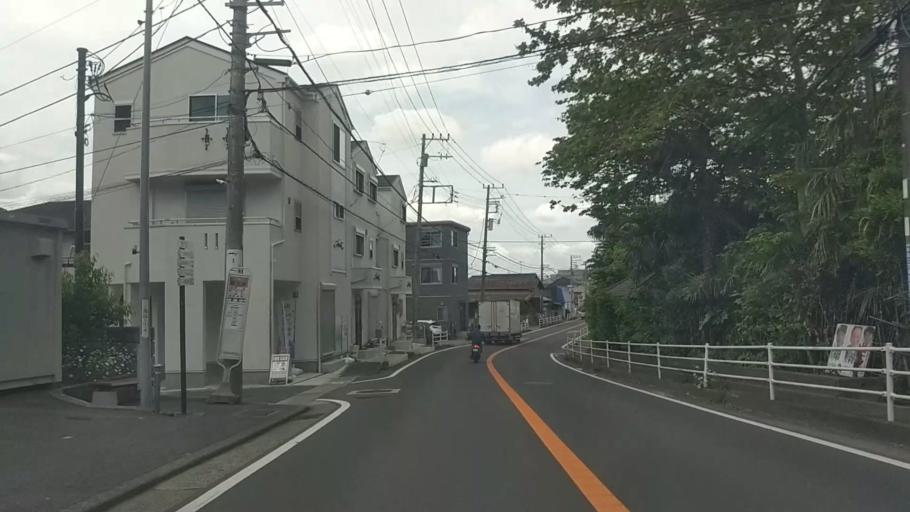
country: JP
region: Kanagawa
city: Fujisawa
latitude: 35.3259
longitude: 139.5084
